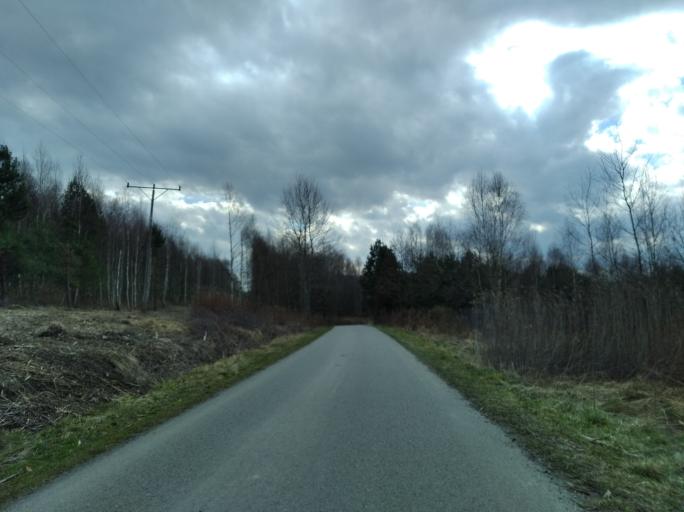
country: PL
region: Subcarpathian Voivodeship
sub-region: Powiat strzyzowski
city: Wysoka Strzyzowska
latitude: 49.7959
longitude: 21.7281
